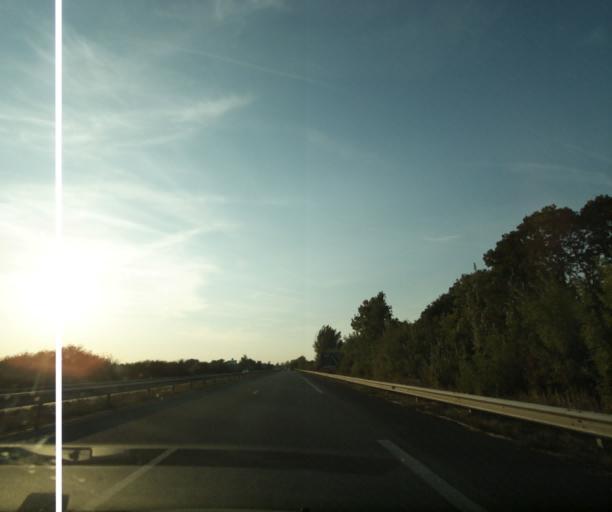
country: FR
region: Midi-Pyrenees
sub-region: Departement du Tarn-et-Garonne
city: Saint-Nicolas-de-la-Grave
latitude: 44.0467
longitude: 0.9899
